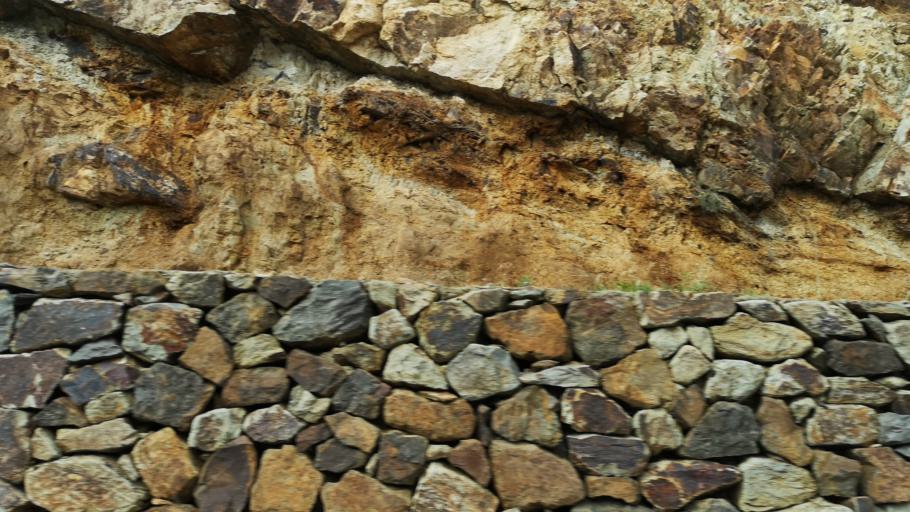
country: ES
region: Canary Islands
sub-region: Provincia de Santa Cruz de Tenerife
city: Vallehermosa
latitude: 28.1724
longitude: -17.2726
